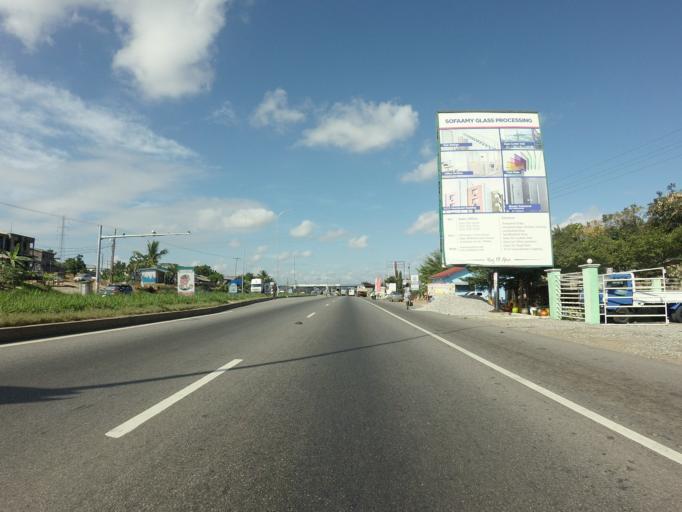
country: GH
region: Central
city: Kasoa
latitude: 5.5486
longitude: -0.3789
